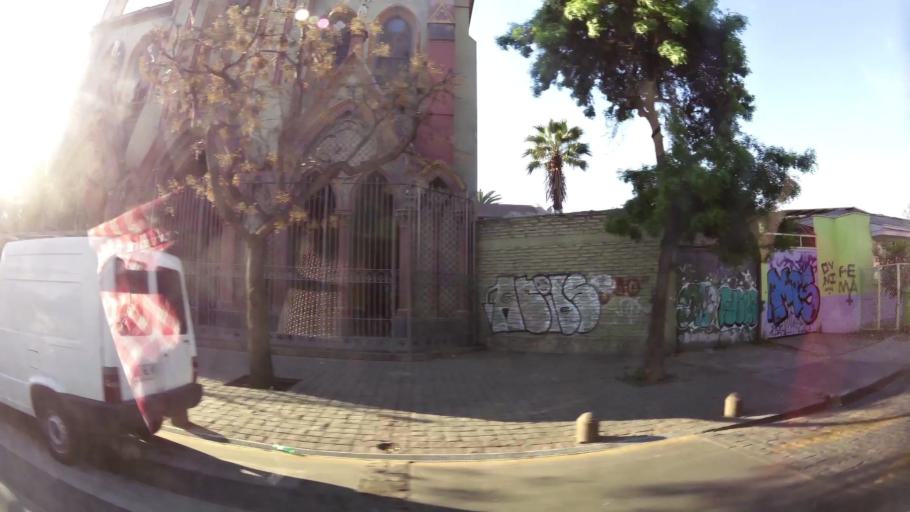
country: CL
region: Santiago Metropolitan
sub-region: Provincia de Santiago
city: Santiago
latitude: -33.4376
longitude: -70.6649
